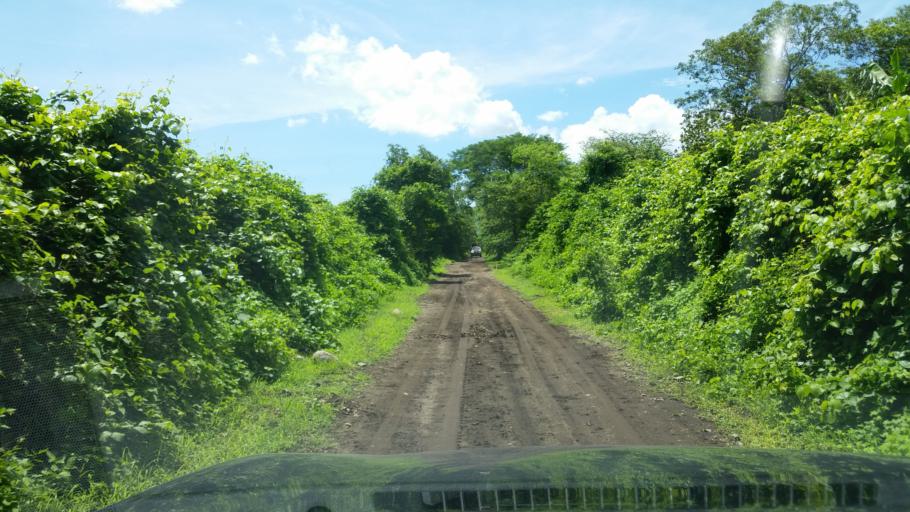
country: NI
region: Chinandega
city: Puerto Morazan
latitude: 12.7611
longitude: -87.1301
